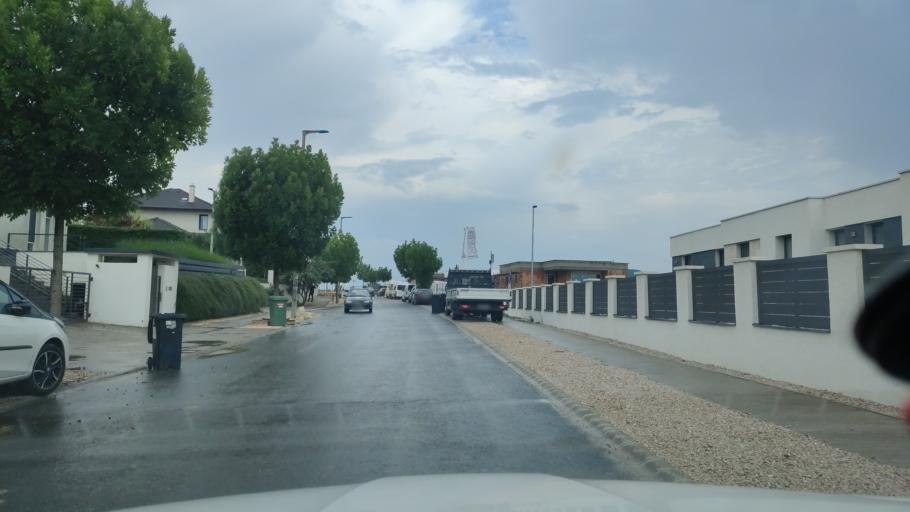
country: HU
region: Pest
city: Toeroekbalint
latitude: 47.4430
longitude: 18.9284
